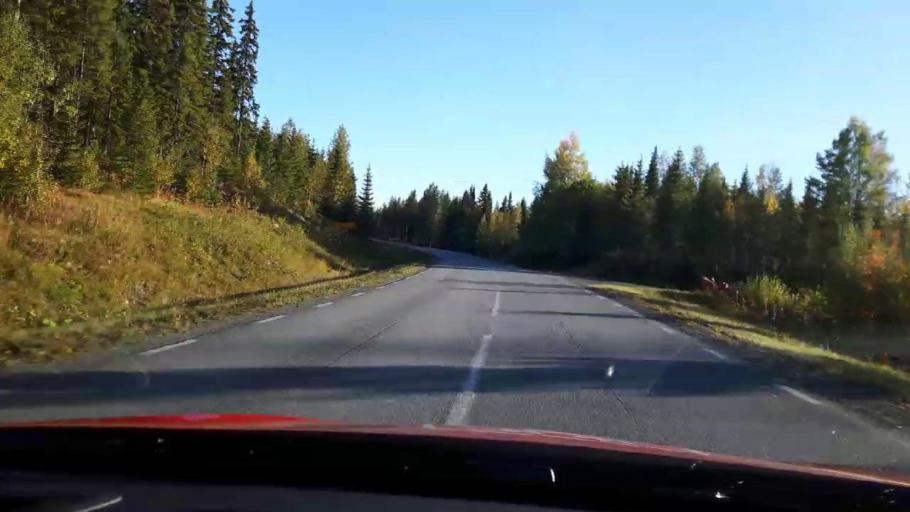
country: SE
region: Jaemtland
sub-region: OEstersunds Kommun
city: Lit
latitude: 63.7934
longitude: 14.7031
